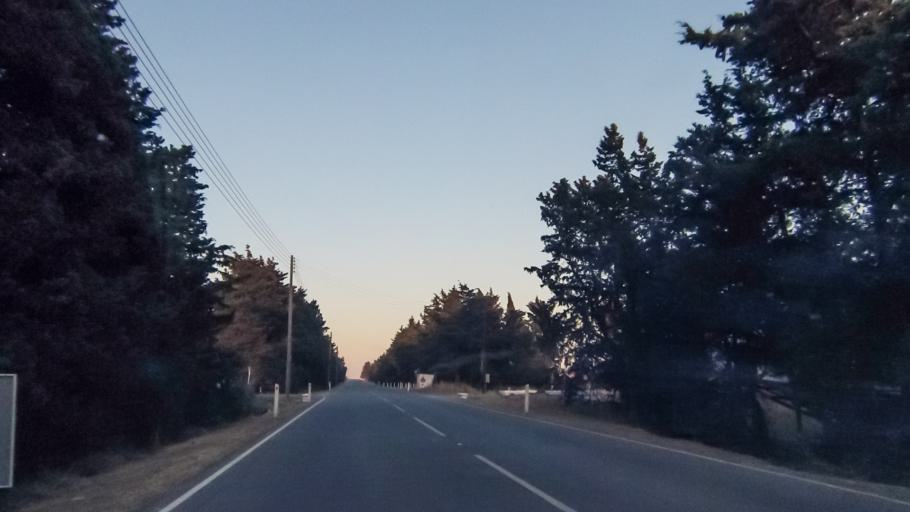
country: CY
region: Limassol
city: Erimi
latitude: 34.6595
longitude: 32.9076
